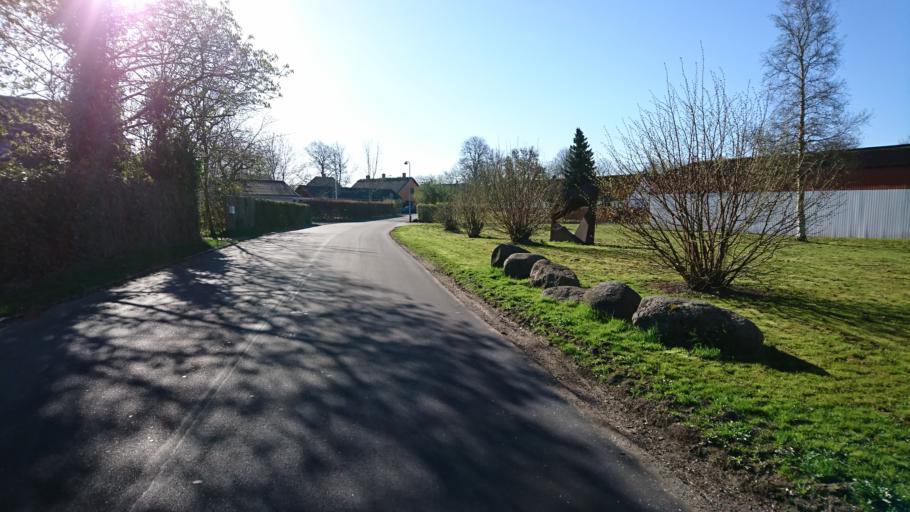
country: DK
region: Capital Region
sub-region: Frederikssund Kommune
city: Skibby
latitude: 55.7246
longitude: 11.9293
